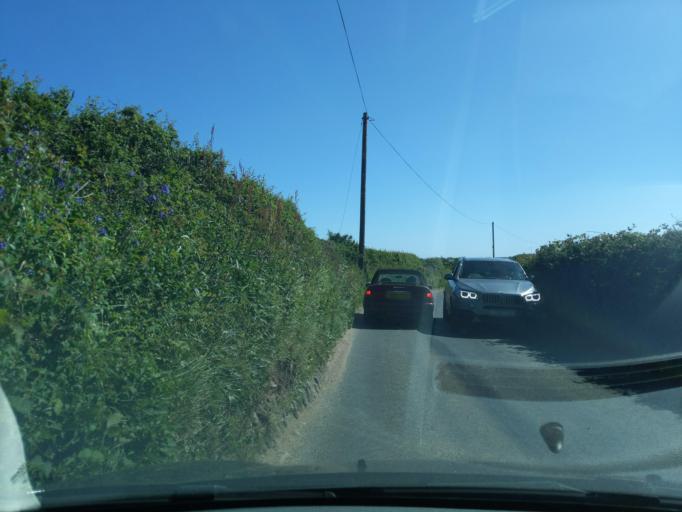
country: GB
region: England
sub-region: Cornwall
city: St. Buryan
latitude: 50.0858
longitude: -5.6038
